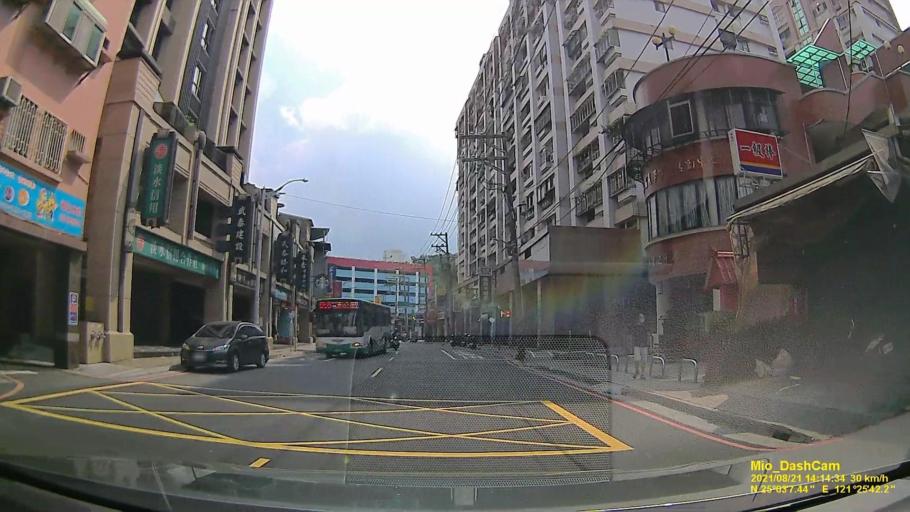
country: TW
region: Taipei
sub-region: Taipei
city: Banqiao
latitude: 25.0521
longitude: 121.4284
